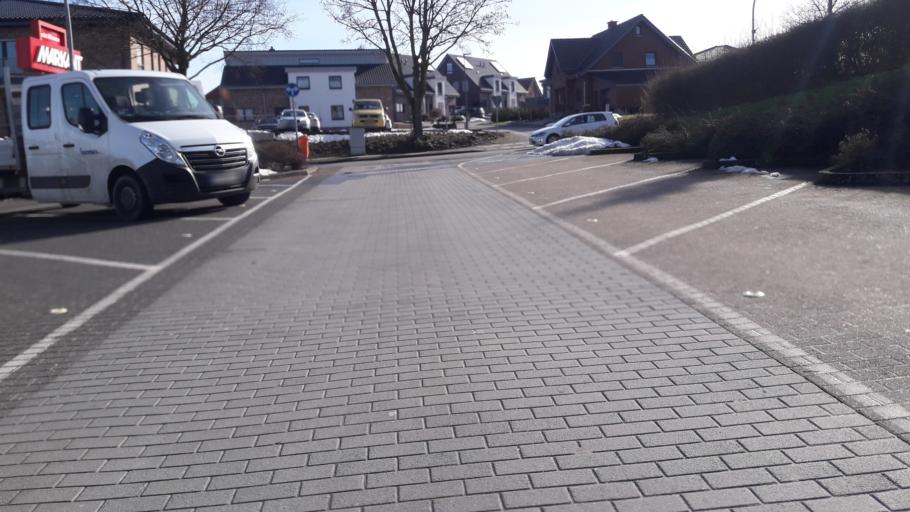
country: DE
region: North Rhine-Westphalia
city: Rietberg
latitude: 51.7543
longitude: 8.4661
